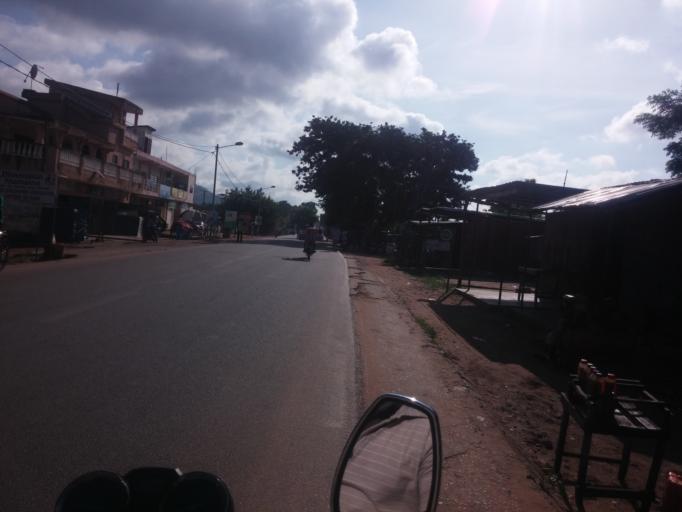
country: TG
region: Kara
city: Kara
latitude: 9.5510
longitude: 1.2022
